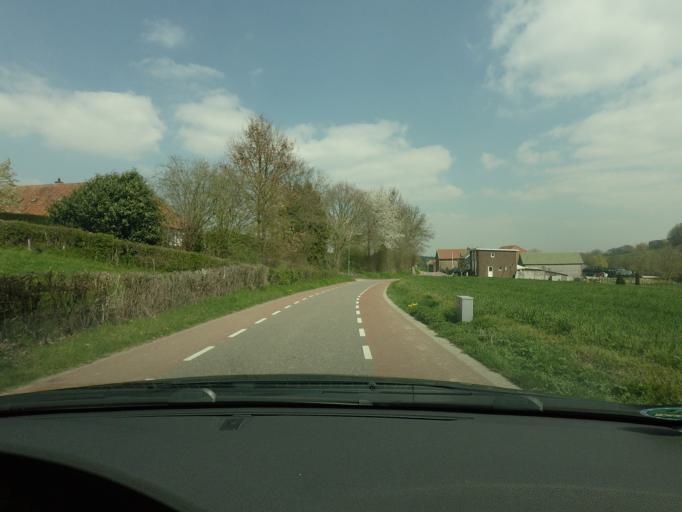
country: NL
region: Limburg
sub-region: Eijsden-Margraten
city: Margraten
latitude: 50.7911
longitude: 5.8583
